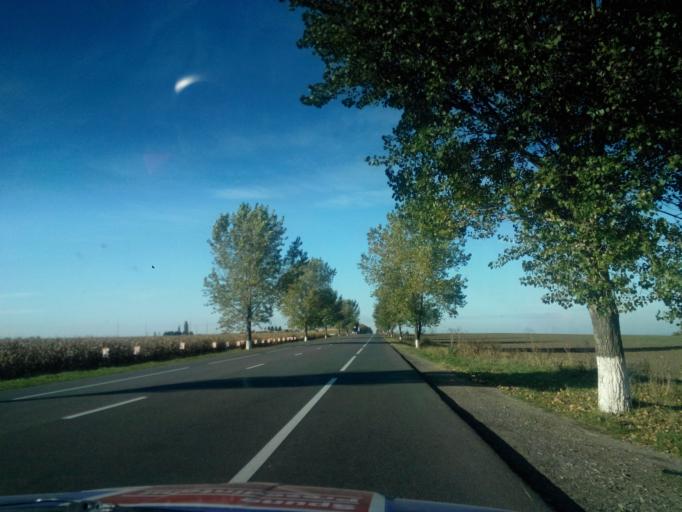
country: RO
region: Bacau
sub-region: Comuna Itesti
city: Itesti
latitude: 46.6498
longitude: 26.9088
